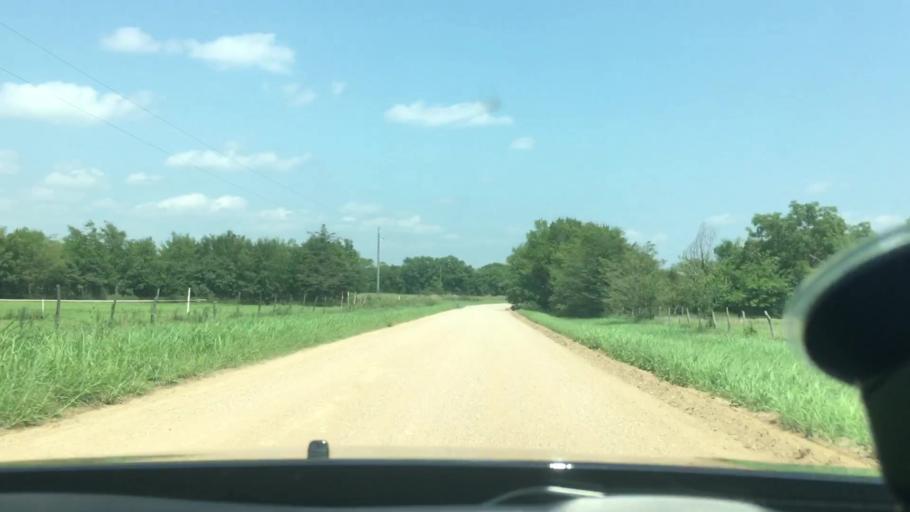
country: US
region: Oklahoma
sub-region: Coal County
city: Coalgate
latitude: 34.4321
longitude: -96.4506
